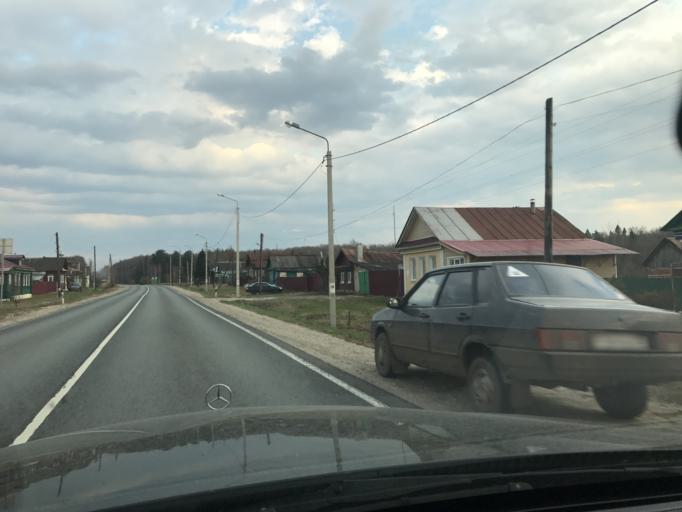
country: RU
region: Vladimir
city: Murom
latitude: 55.6387
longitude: 41.8560
